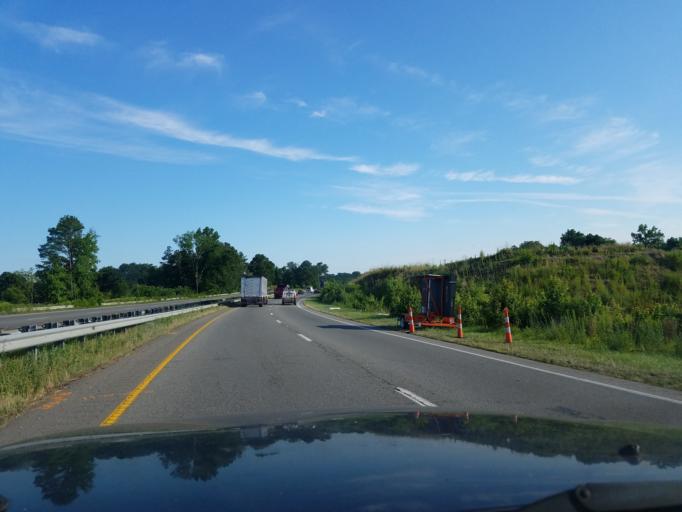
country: US
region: North Carolina
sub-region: Durham County
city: Durham
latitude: 35.9875
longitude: -78.8620
